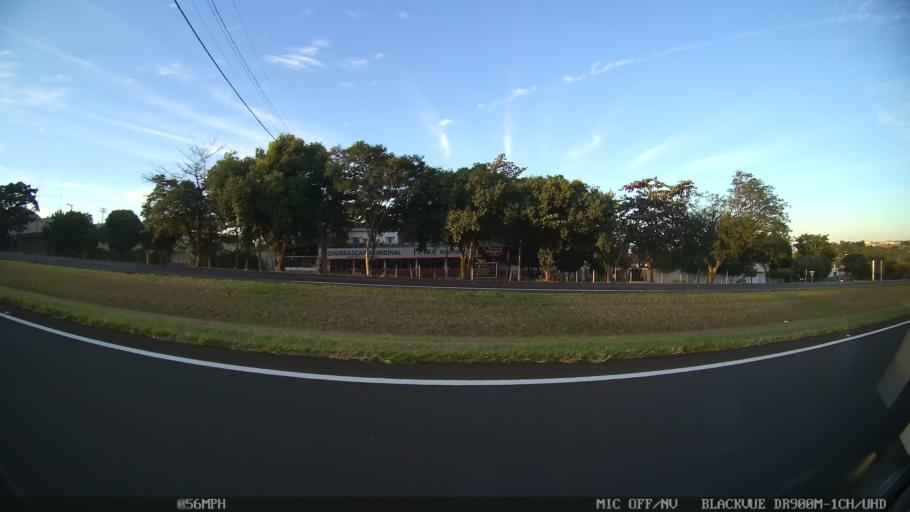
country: BR
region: Sao Paulo
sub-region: Catanduva
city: Catanduva
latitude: -21.1585
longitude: -48.9883
